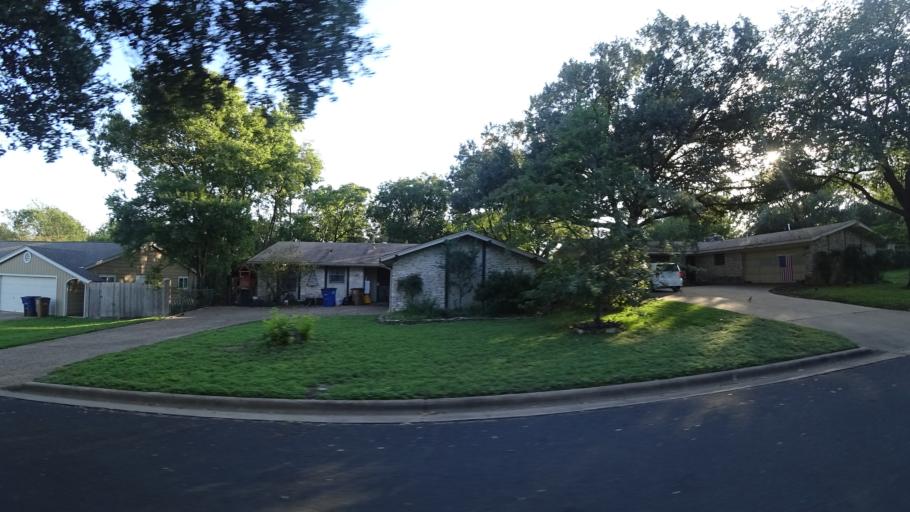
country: US
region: Texas
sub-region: Travis County
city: Wells Branch
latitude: 30.3606
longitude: -97.7023
